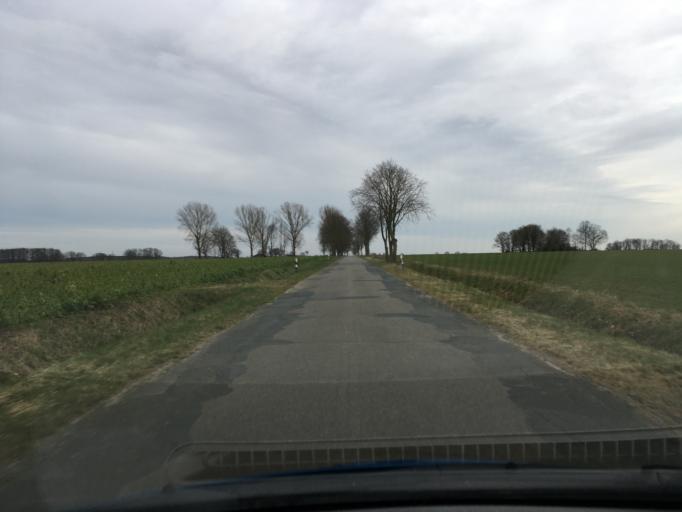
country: DE
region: Lower Saxony
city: Ratzlingen
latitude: 52.9937
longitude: 10.6550
